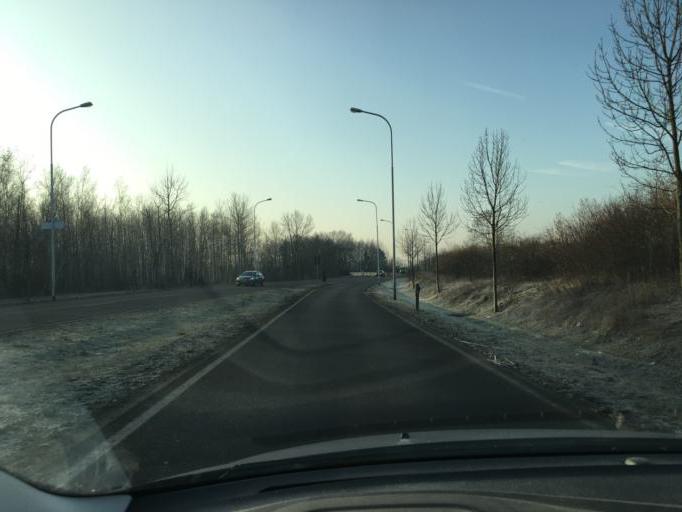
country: DE
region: Saxony-Anhalt
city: Halle (Saale)
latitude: 51.4547
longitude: 11.9955
